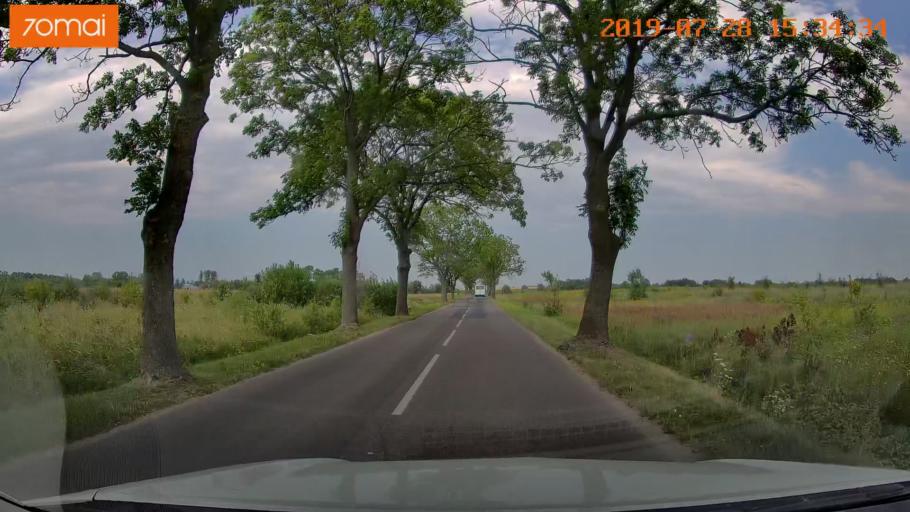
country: RU
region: Kaliningrad
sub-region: Gorod Kaliningrad
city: Yantarnyy
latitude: 54.8808
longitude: 19.9706
